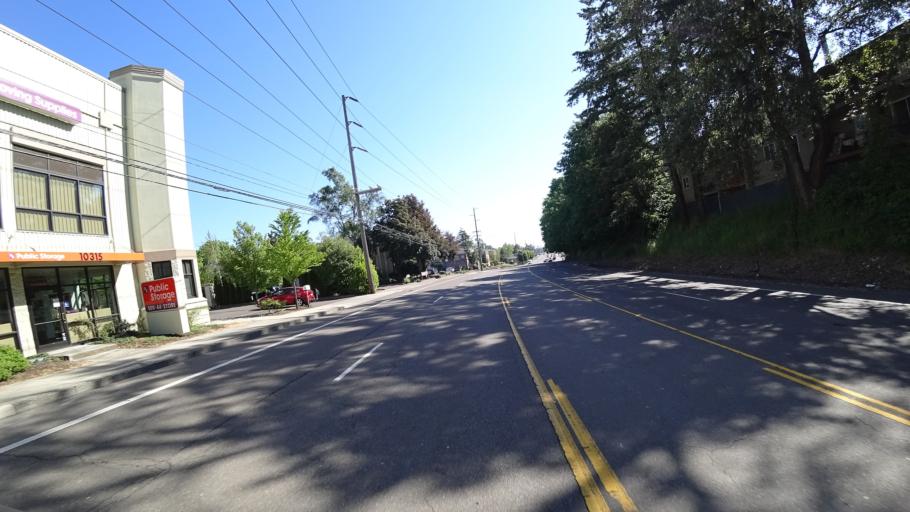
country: US
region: Oregon
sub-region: Washington County
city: Metzger
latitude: 45.4512
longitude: -122.7269
